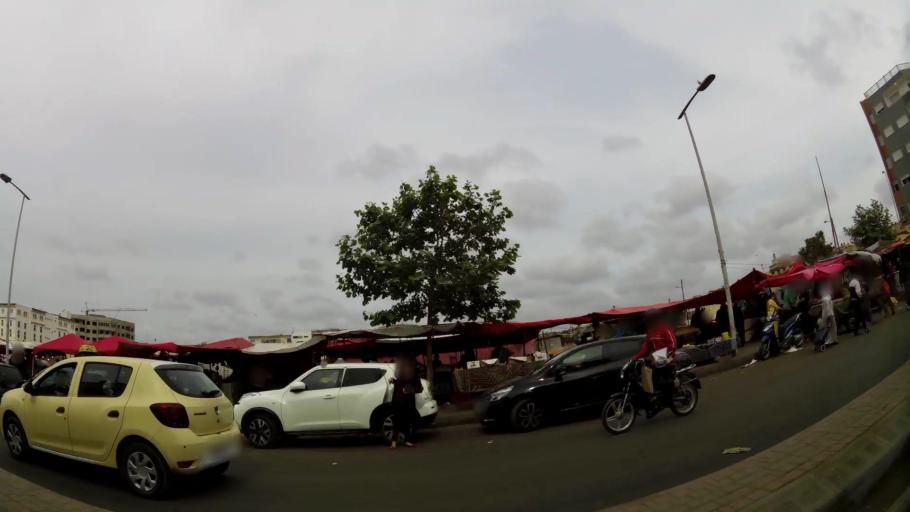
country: MA
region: Rabat-Sale-Zemmour-Zaer
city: Sale
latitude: 34.0434
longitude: -6.8066
